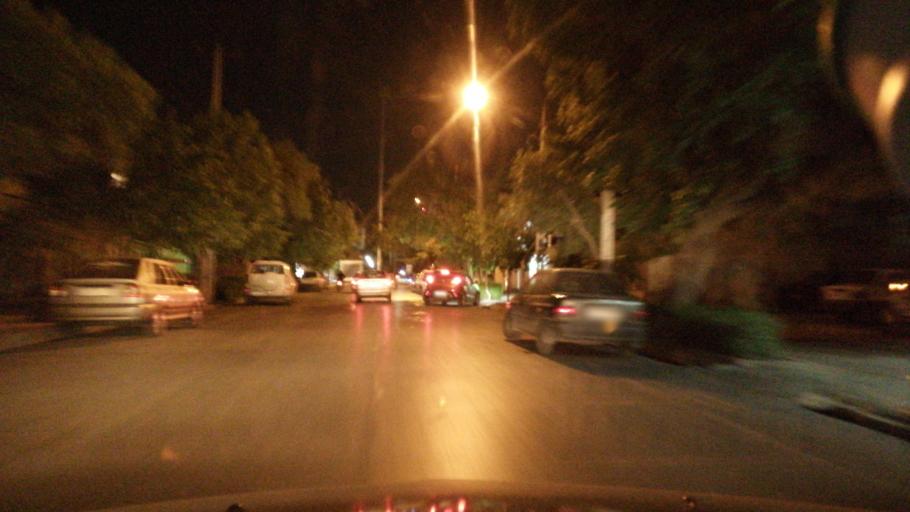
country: IR
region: Razavi Khorasan
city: Mashhad
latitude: 36.3050
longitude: 59.6012
